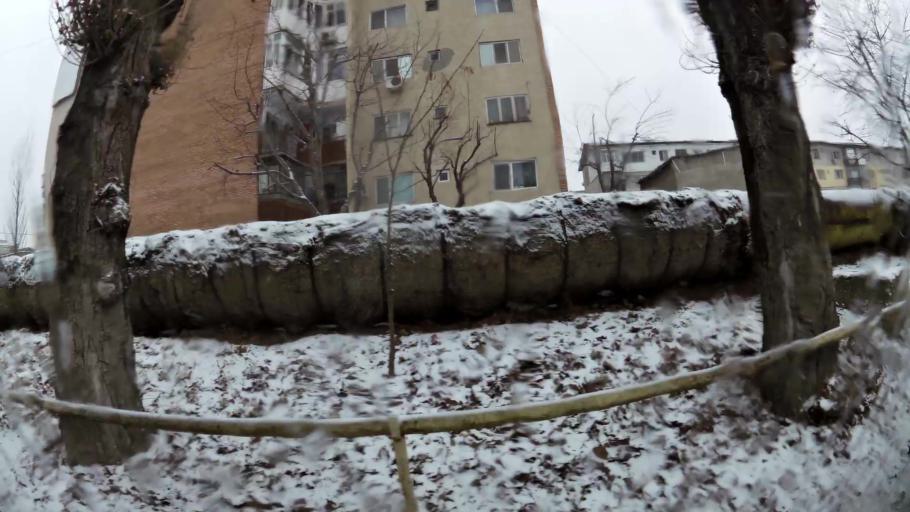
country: RO
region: Dambovita
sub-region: Municipiul Targoviste
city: Targoviste
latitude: 44.9296
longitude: 25.4464
